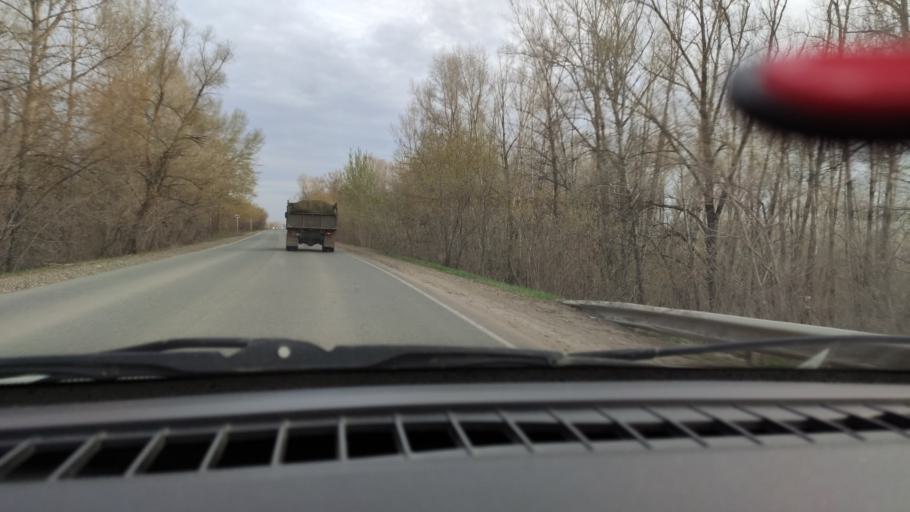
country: RU
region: Orenburg
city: Tatarskaya Kargala
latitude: 51.9315
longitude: 55.1737
